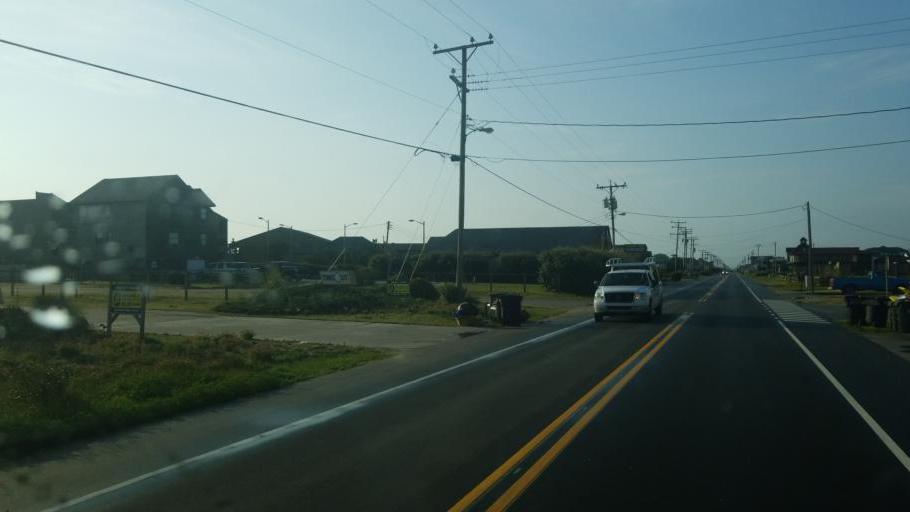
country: US
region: North Carolina
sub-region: Dare County
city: Kill Devil Hills
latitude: 36.0136
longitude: -75.6571
